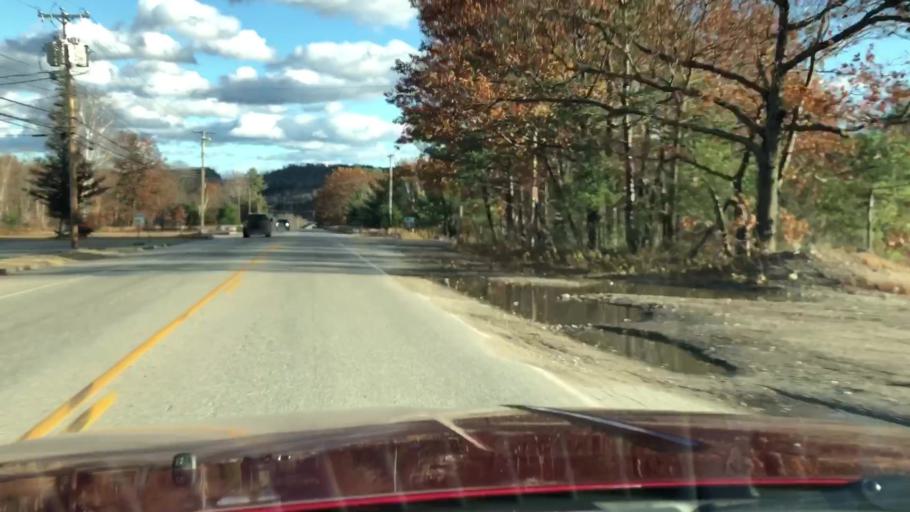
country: US
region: Maine
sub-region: Oxford County
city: Mexico
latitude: 44.5352
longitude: -70.5075
